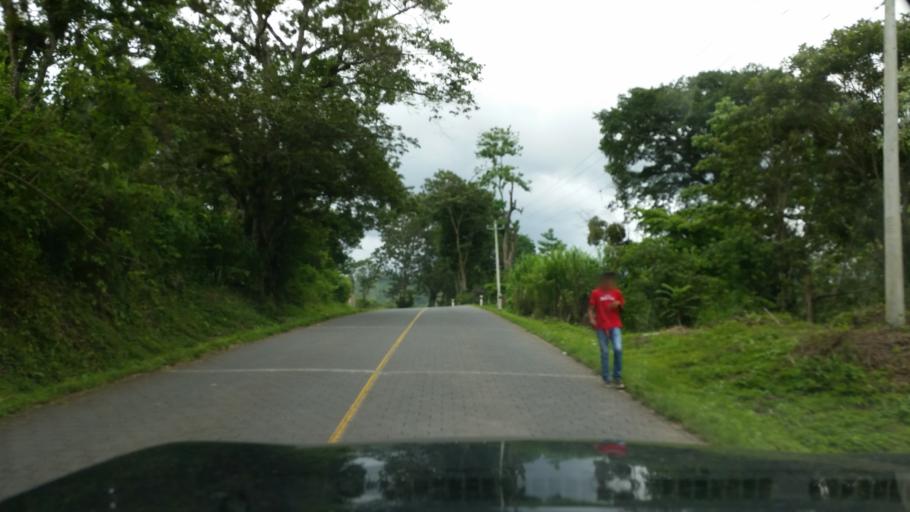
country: NI
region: Jinotega
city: Jinotega
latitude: 13.1878
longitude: -85.7328
